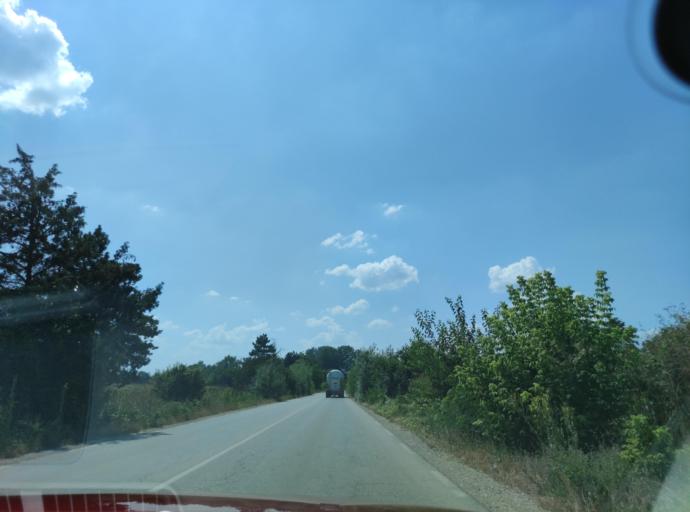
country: BG
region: Pleven
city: Iskur
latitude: 43.4533
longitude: 24.2484
